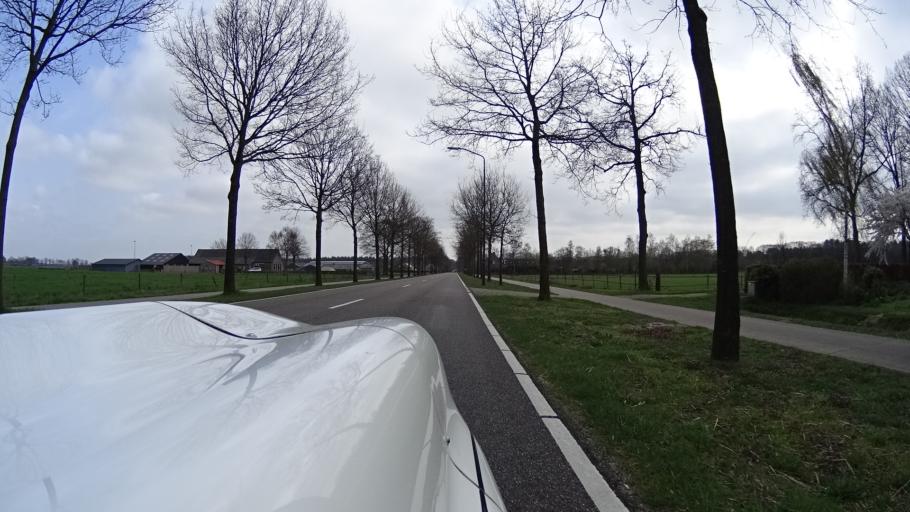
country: NL
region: North Brabant
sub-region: Gemeente Veghel
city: Zijtaart
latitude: 51.5475
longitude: 5.5506
